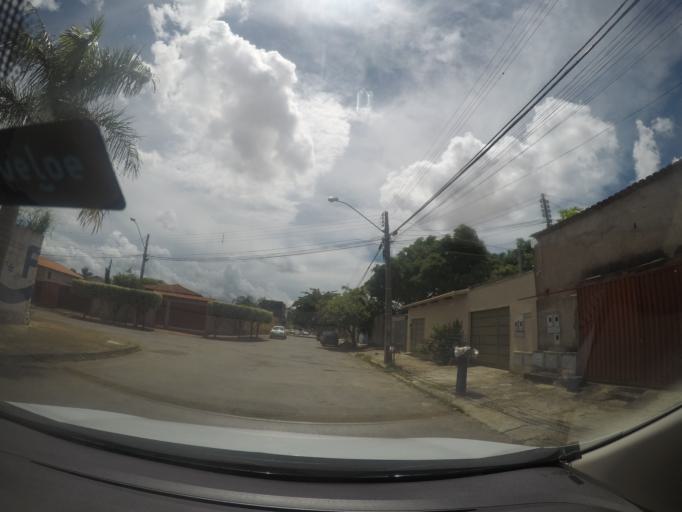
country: BR
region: Goias
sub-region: Goiania
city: Goiania
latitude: -16.6776
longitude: -49.3141
